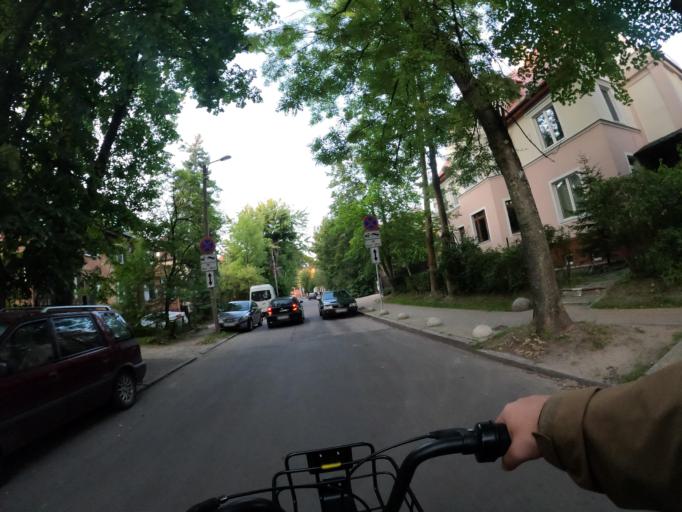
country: RU
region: Kaliningrad
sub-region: Gorod Kaliningrad
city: Kaliningrad
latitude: 54.7206
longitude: 20.4688
